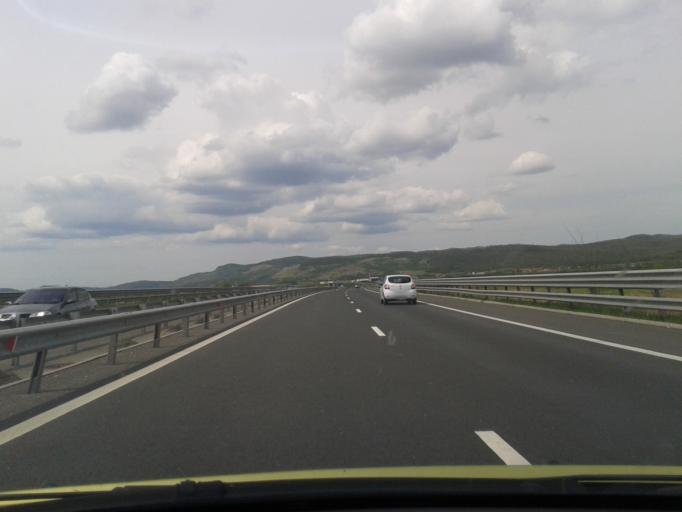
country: RO
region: Hunedoara
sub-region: Comuna Harau
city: Harau
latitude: 45.8991
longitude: 22.9336
